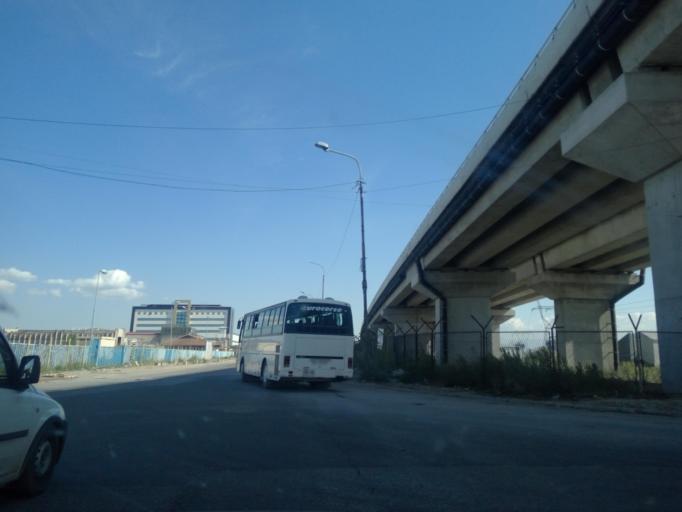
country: XK
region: Pristina
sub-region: Kosovo Polje
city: Kosovo Polje
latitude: 42.6486
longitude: 21.1218
